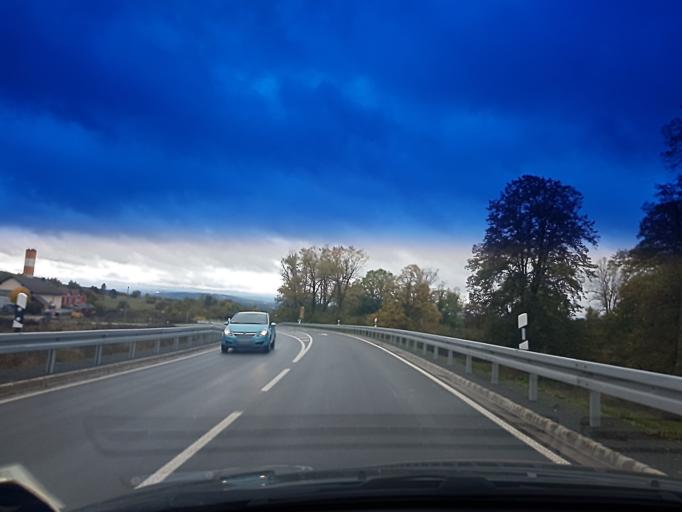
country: DE
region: Bavaria
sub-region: Upper Franconia
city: Bindlach
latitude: 49.9952
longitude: 11.6228
